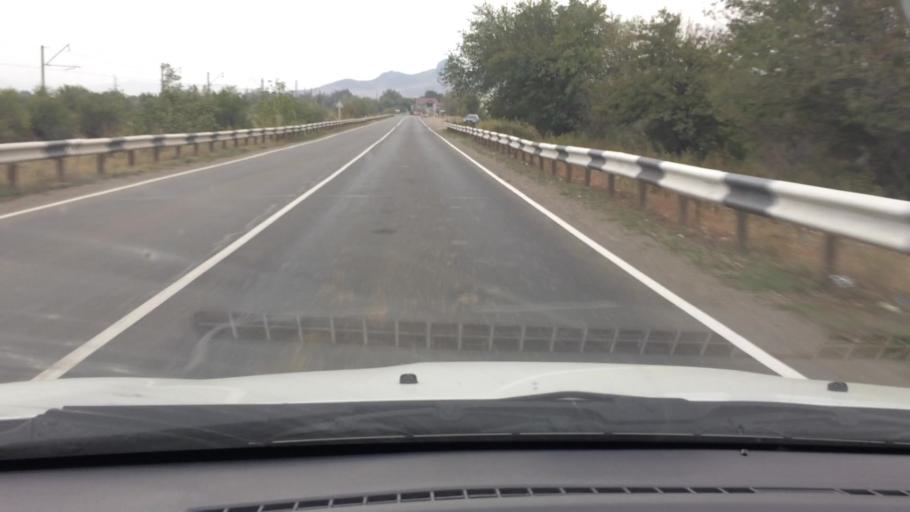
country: GE
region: Kvemo Kartli
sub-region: Marneuli
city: Marneuli
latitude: 41.4077
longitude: 44.8312
